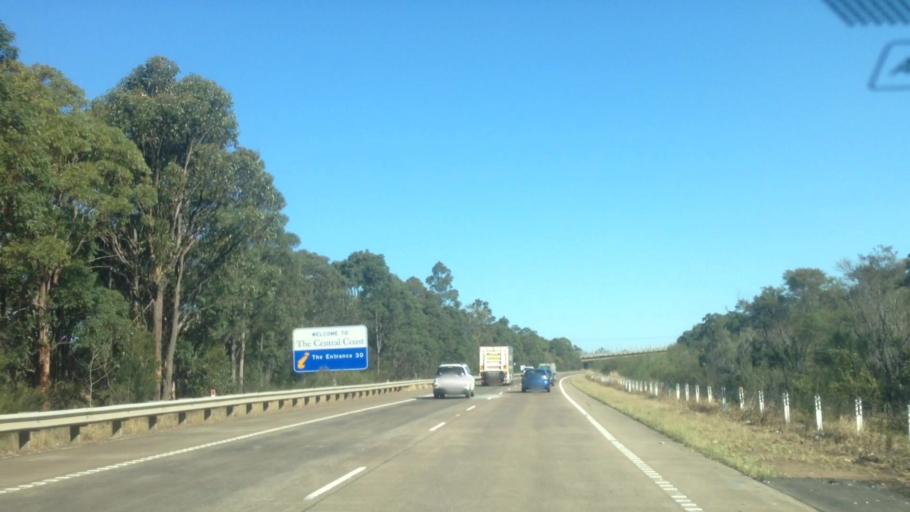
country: AU
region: New South Wales
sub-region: Wyong Shire
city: Charmhaven
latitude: -33.1890
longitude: 151.4674
